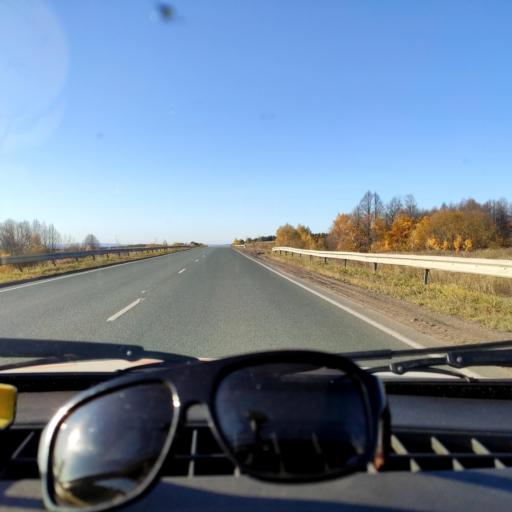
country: RU
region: Bashkortostan
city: Blagoveshchensk
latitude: 55.0944
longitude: 55.8151
